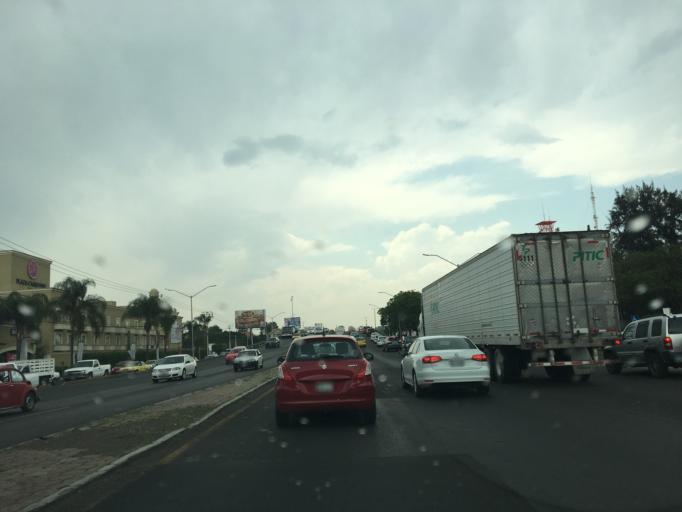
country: MX
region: Queretaro
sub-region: Queretaro
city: Santiago de Queretaro
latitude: 20.5804
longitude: -100.4057
